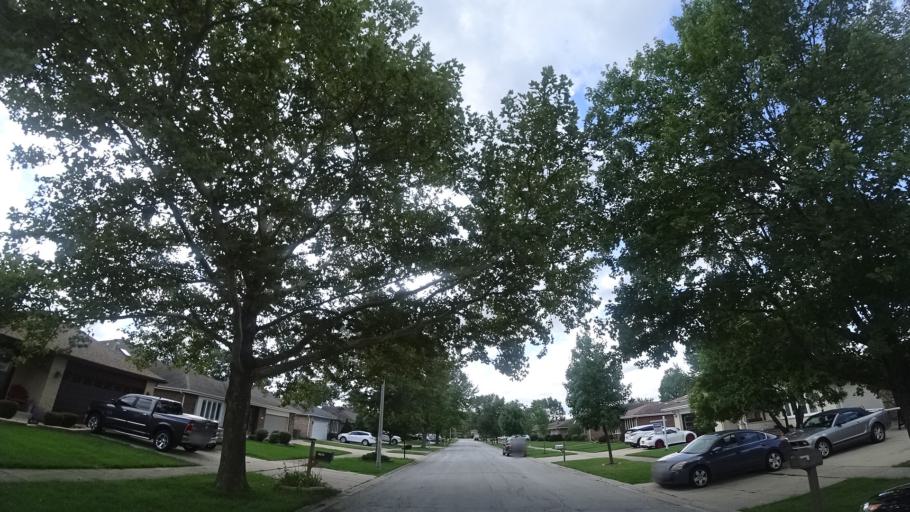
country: US
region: Illinois
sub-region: Cook County
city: Tinley Park
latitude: 41.5679
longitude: -87.7756
